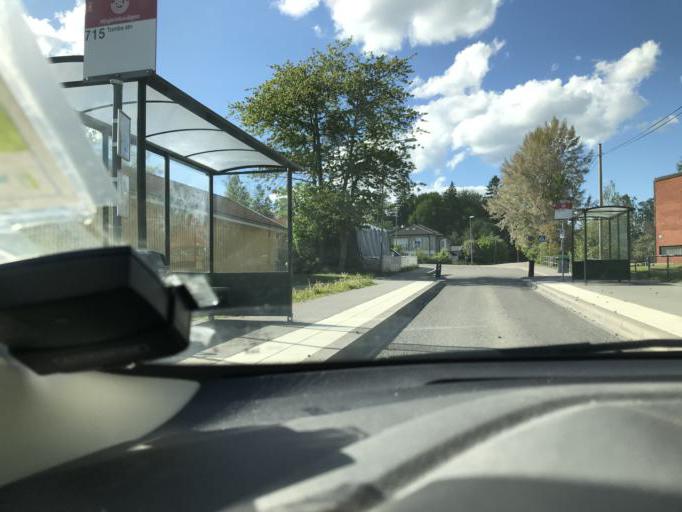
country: SE
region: Stockholm
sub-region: Botkyrka Kommun
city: Tumba
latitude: 59.1975
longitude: 17.8236
